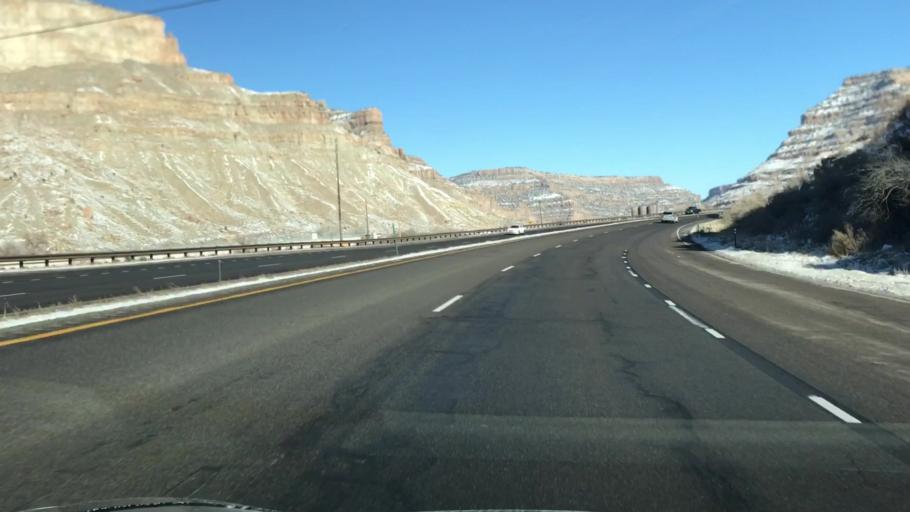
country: US
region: Colorado
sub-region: Mesa County
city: Palisade
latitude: 39.1464
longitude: -108.3143
